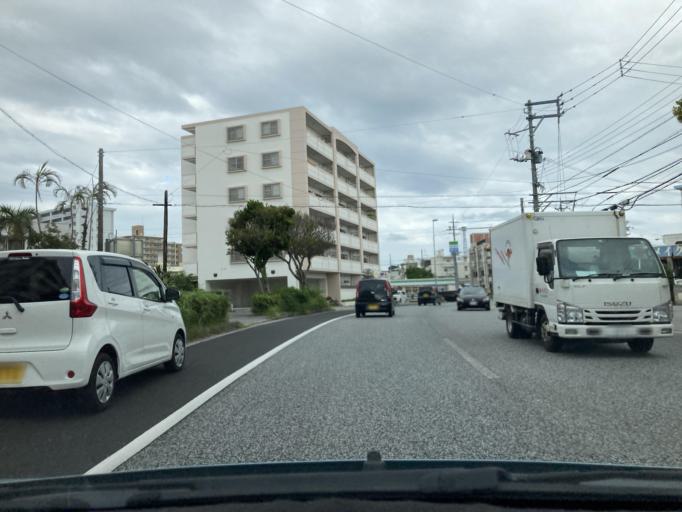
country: JP
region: Okinawa
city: Ginowan
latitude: 26.2546
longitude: 127.7559
